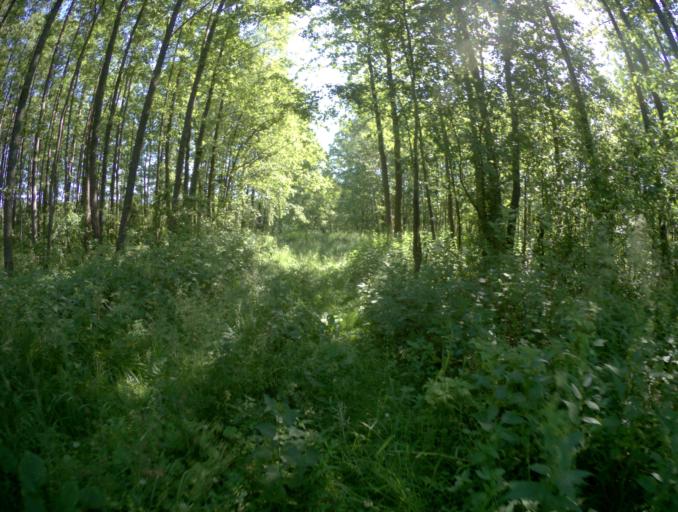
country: RU
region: Vladimir
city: Vyazniki
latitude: 56.2973
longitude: 42.3183
